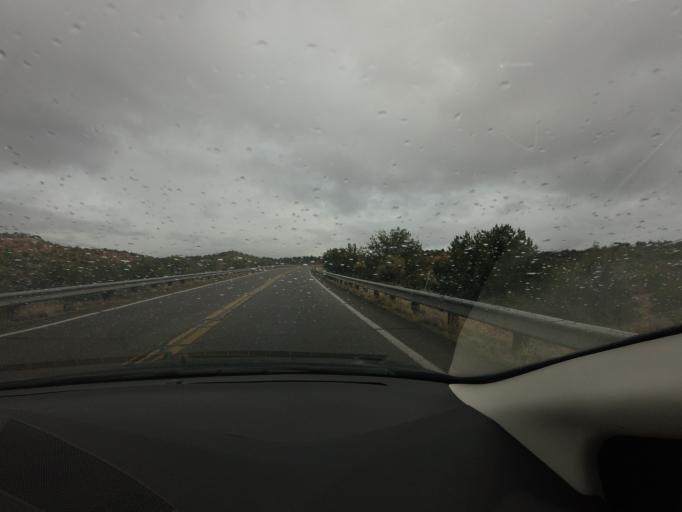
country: US
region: Arizona
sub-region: Yavapai County
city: Cornville
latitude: 34.7000
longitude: -111.8634
